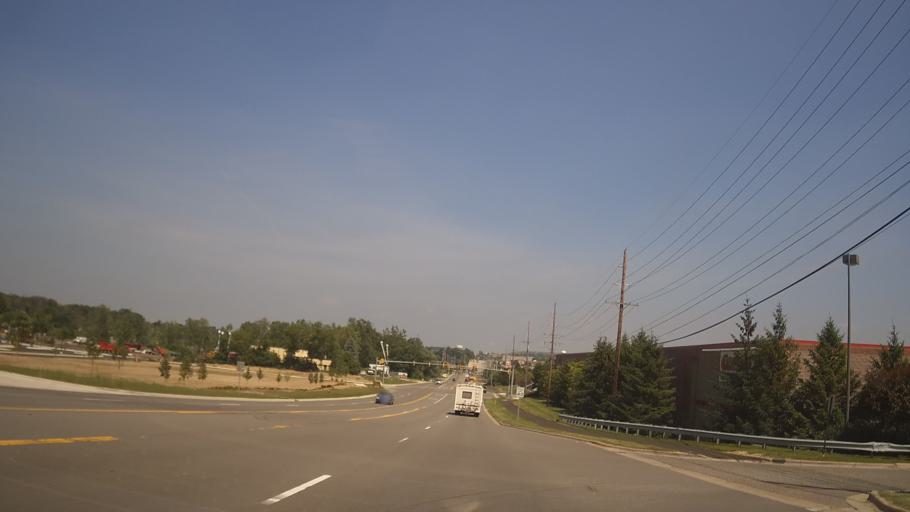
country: US
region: Michigan
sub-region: Oakland County
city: Auburn Hills
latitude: 42.7073
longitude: -83.2985
